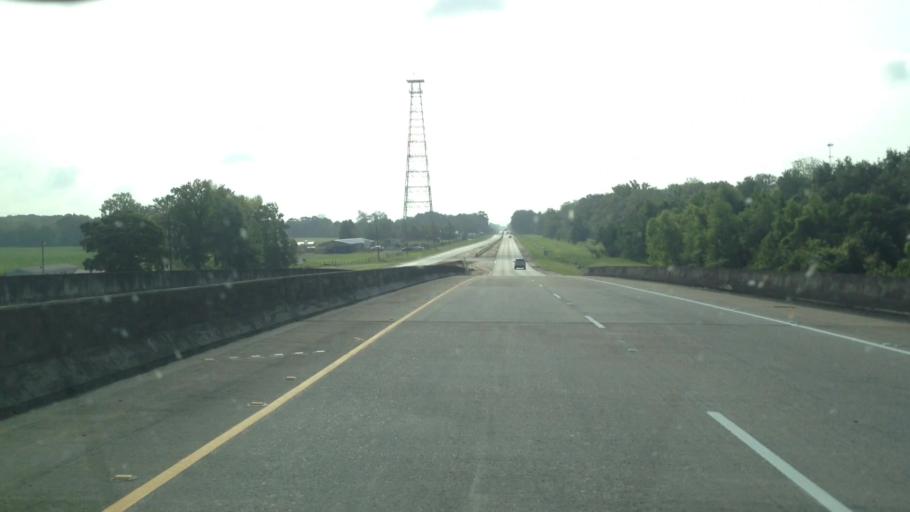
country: US
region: Louisiana
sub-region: Pointe Coupee Parish
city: Livonia
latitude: 30.5552
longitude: -91.5777
